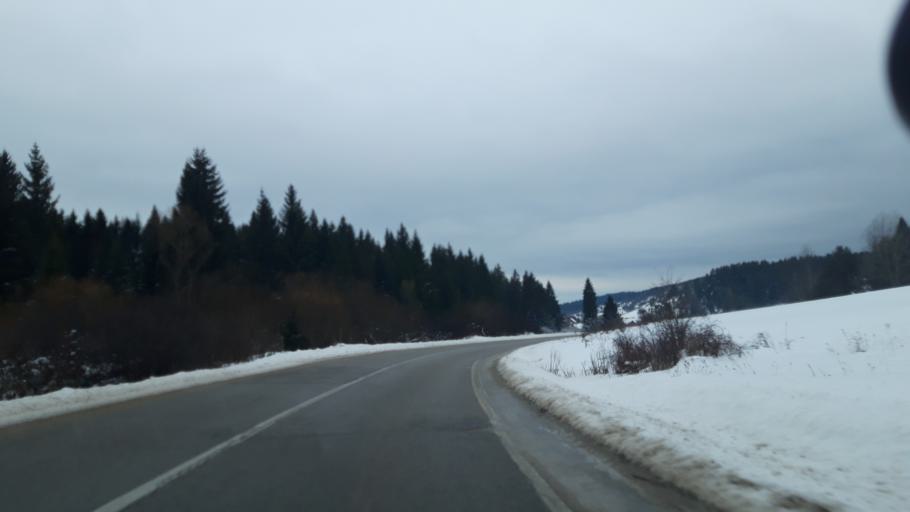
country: BA
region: Republika Srpska
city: Han Pijesak
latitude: 44.0037
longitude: 18.8888
